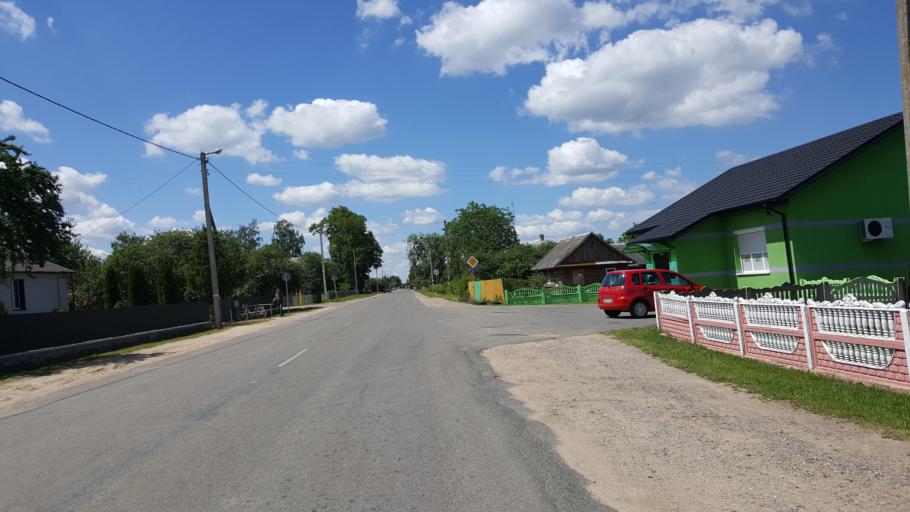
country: PL
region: Podlasie
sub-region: Powiat hajnowski
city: Czeremcha
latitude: 52.4897
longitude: 23.4475
